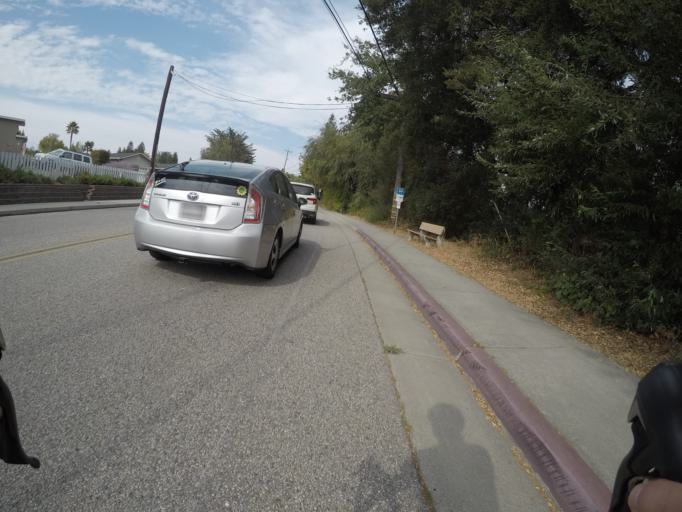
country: US
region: California
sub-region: Santa Cruz County
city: Scotts Valley
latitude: 37.0649
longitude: -122.0052
